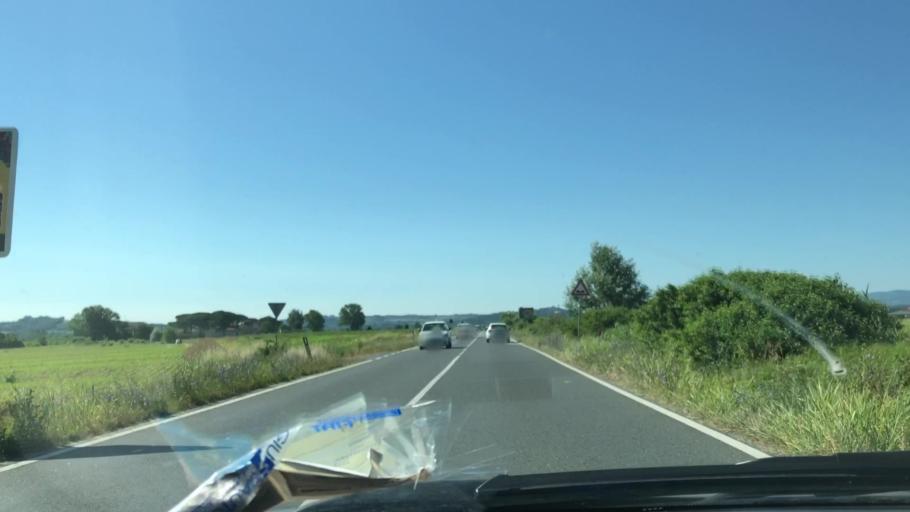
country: IT
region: Tuscany
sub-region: Province of Pisa
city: Forcoli
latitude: 43.5949
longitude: 10.6983
